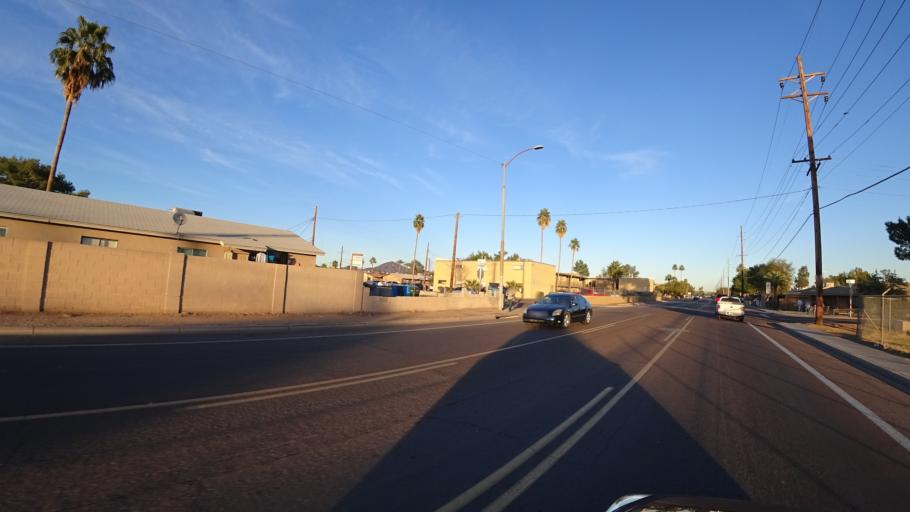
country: US
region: Arizona
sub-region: Maricopa County
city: Phoenix
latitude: 33.4585
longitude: -112.0221
